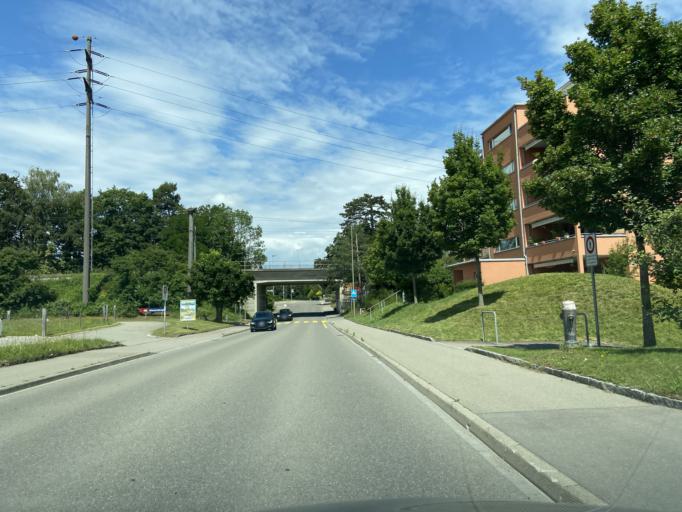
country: CH
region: Zurich
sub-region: Bezirk Winterthur
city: Wiesendangen / Wiesendangen (Dorf)
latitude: 47.5261
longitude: 8.7776
